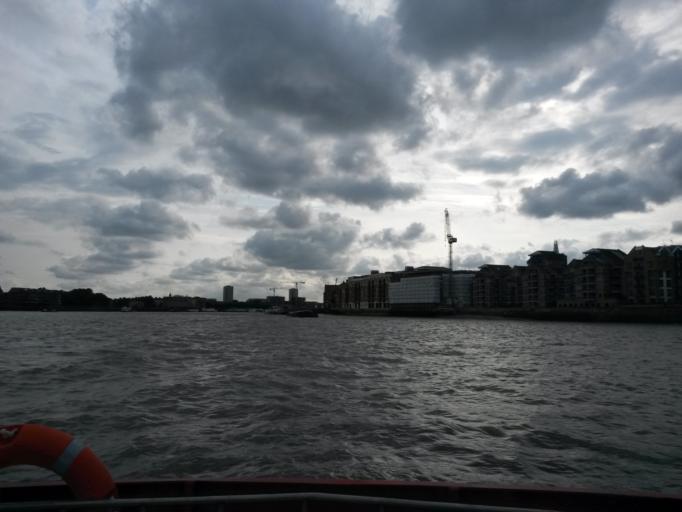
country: GB
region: England
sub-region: Greater London
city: Bethnal Green
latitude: 51.5050
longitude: -0.0516
